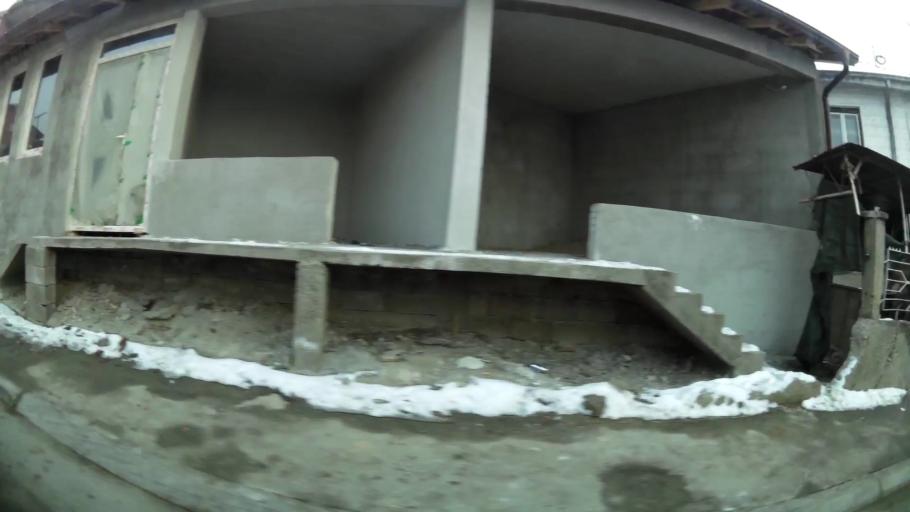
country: MK
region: Suto Orizari
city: Suto Orizare
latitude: 42.0370
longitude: 21.4266
